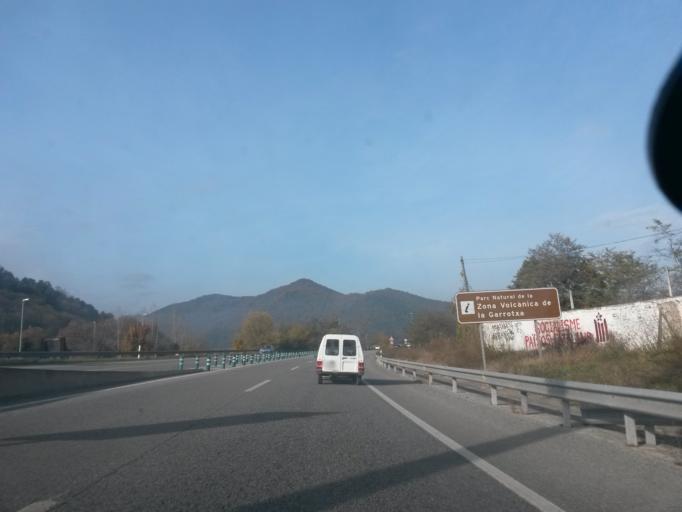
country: ES
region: Catalonia
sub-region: Provincia de Girona
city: MeteOlot
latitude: 42.1949
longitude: 2.5031
